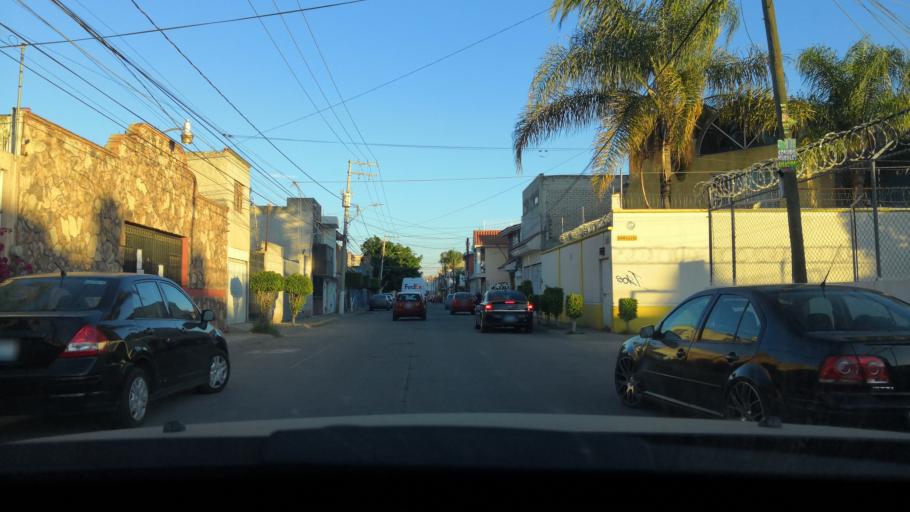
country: MX
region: Guanajuato
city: Leon
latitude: 21.1659
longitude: -101.6609
